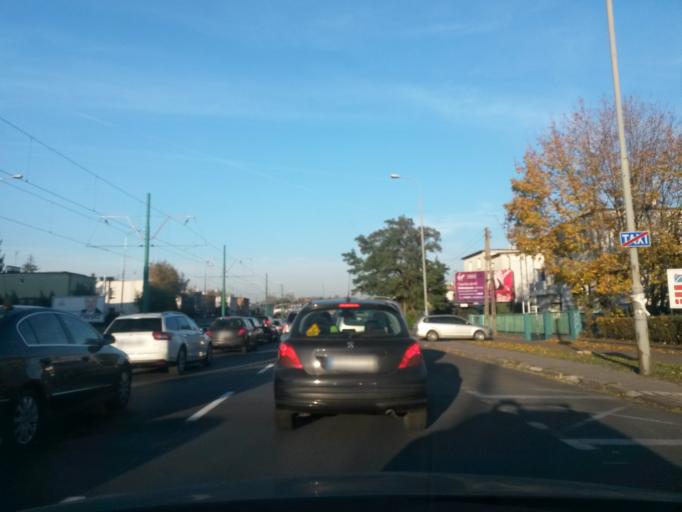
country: PL
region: Greater Poland Voivodeship
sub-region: Powiat poznanski
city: Lubon
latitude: 52.3940
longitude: 16.8607
